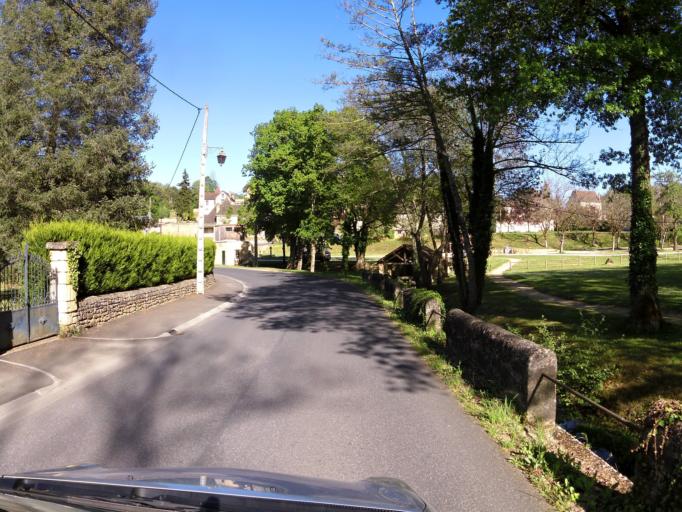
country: FR
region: Aquitaine
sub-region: Departement de la Dordogne
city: Carsac-Aillac
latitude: 44.8405
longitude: 1.2732
